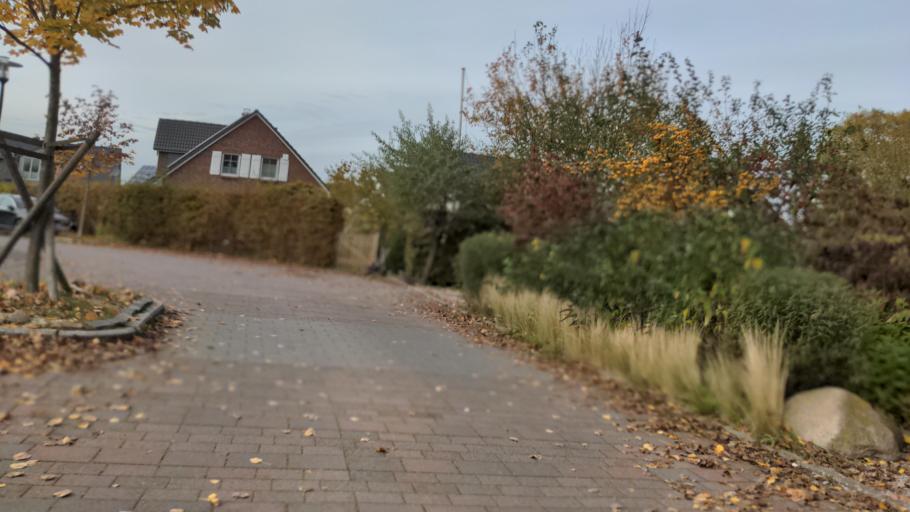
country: DE
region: Schleswig-Holstein
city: Stockelsdorf
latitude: 53.9089
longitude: 10.6614
